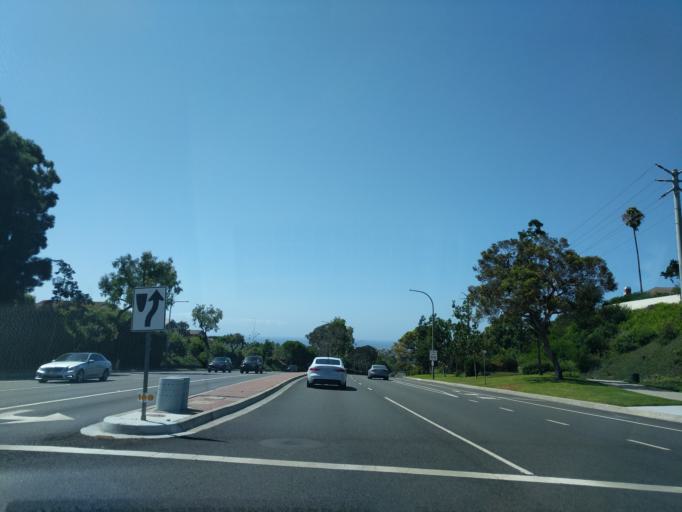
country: US
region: California
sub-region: Orange County
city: San Joaquin Hills
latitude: 33.6075
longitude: -117.8510
